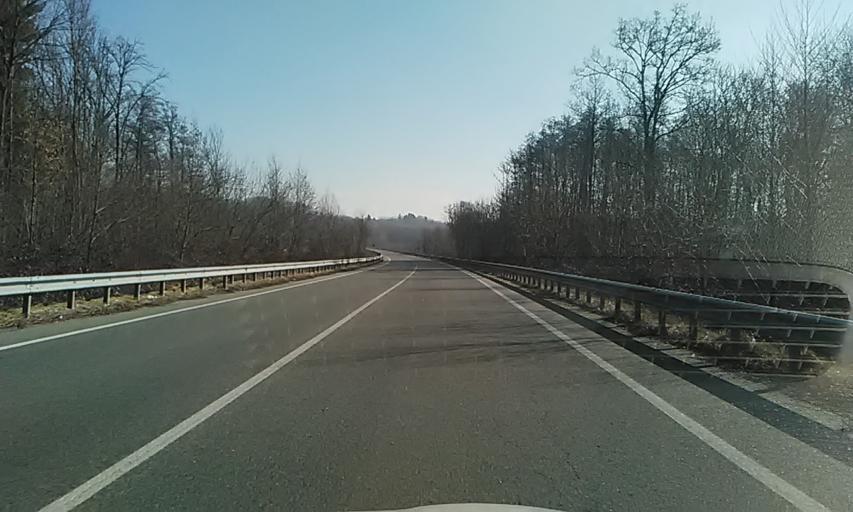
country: IT
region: Piedmont
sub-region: Provincia di Novara
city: Prato Sesia
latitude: 45.6609
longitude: 8.3702
